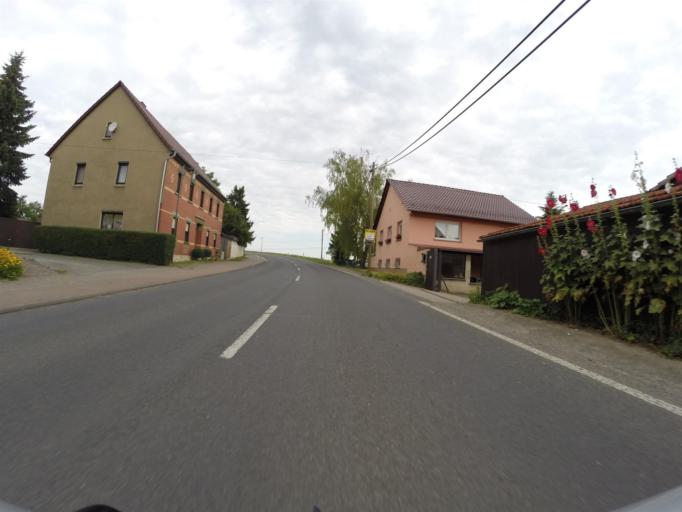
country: DE
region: Thuringia
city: Ramsla
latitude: 51.0525
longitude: 11.2858
